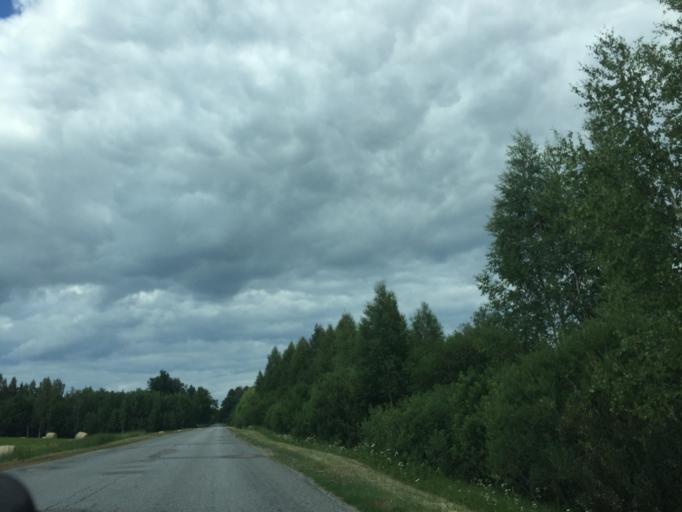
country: LV
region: Skriveri
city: Skriveri
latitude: 56.8260
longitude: 25.1244
